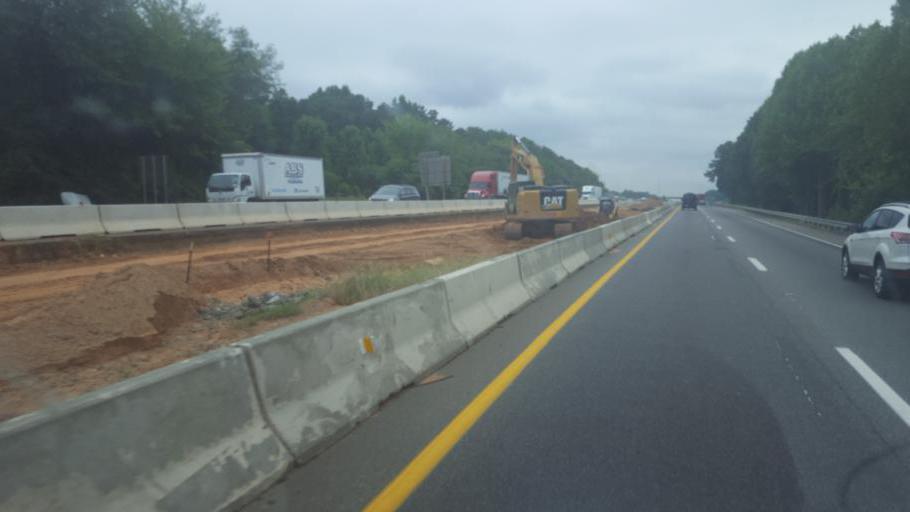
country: US
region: North Carolina
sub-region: Gaston County
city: Davidson
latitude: 35.5196
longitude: -80.8647
